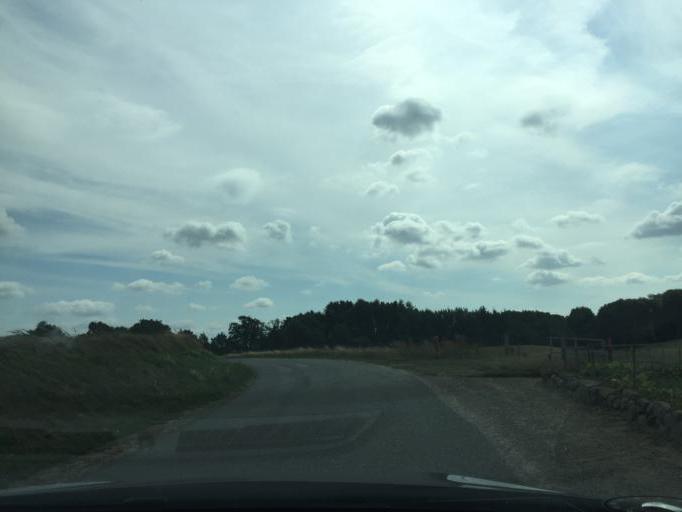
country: DK
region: South Denmark
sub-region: Assens Kommune
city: Tommerup Stationsby
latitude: 55.4014
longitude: 10.2362
